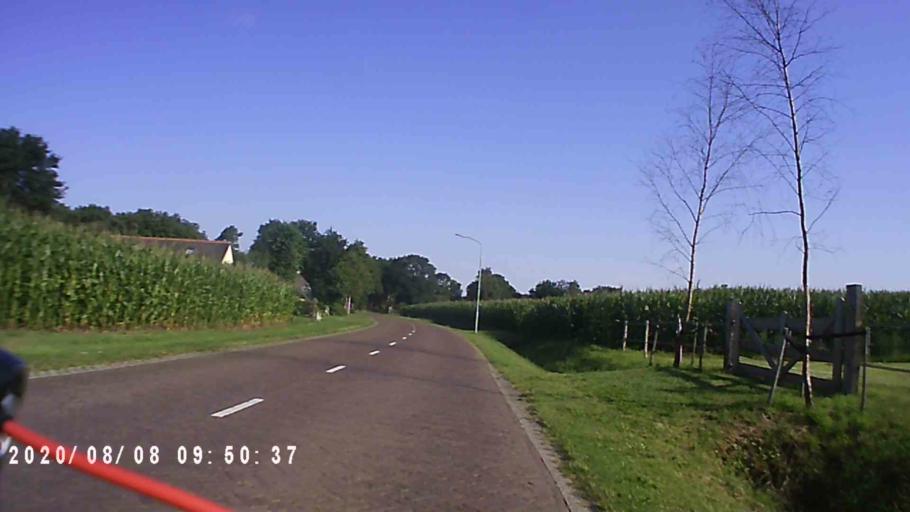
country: NL
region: Groningen
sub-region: Gemeente Leek
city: Leek
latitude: 53.0860
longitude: 6.3884
